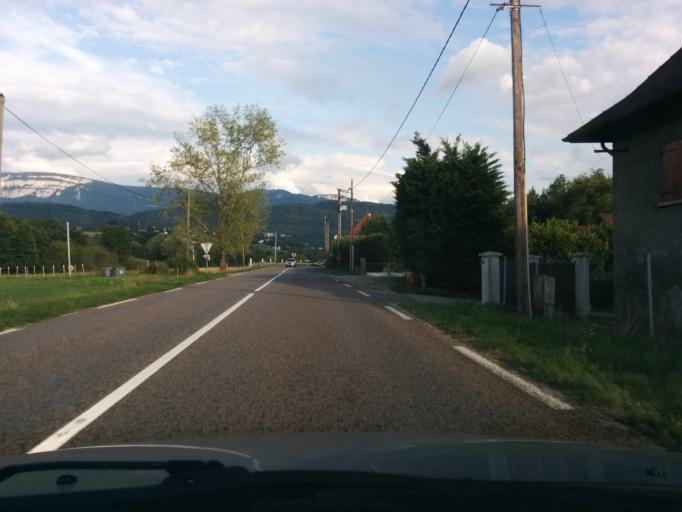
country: FR
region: Rhone-Alpes
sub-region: Departement de la Savoie
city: Domessin
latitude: 45.5221
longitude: 5.7020
